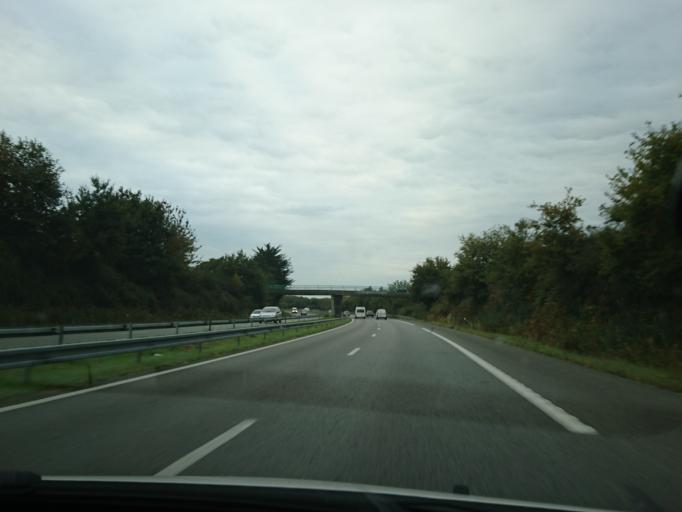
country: FR
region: Brittany
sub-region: Departement du Morbihan
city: Theix
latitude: 47.6284
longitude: -2.6359
